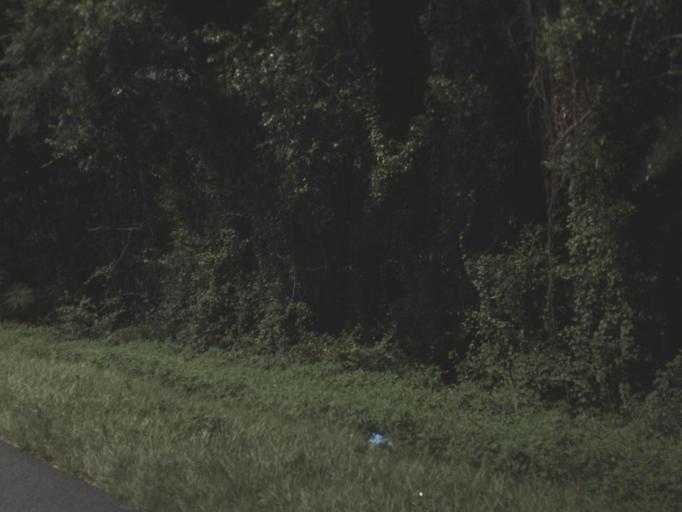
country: US
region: Florida
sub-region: Citrus County
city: Beverly Hills
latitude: 28.9610
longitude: -82.4172
